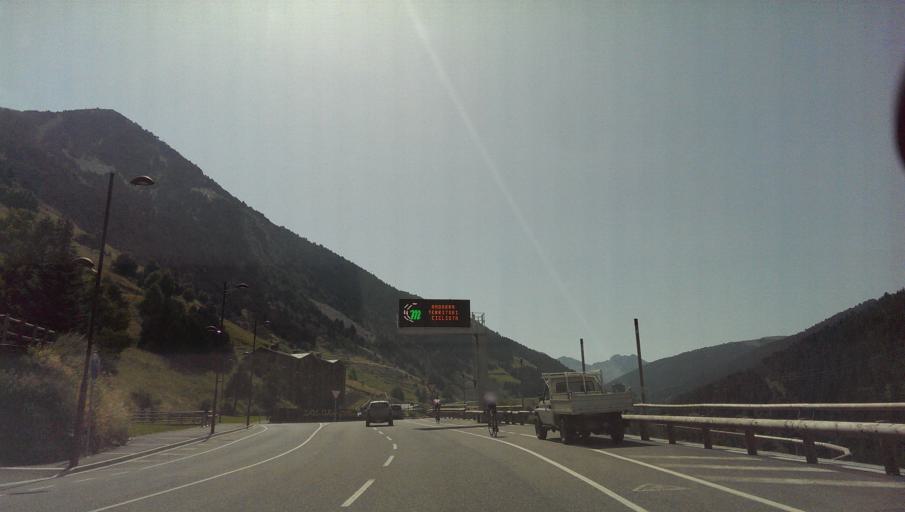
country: AD
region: Canillo
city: El Tarter
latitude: 42.5746
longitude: 1.6729
